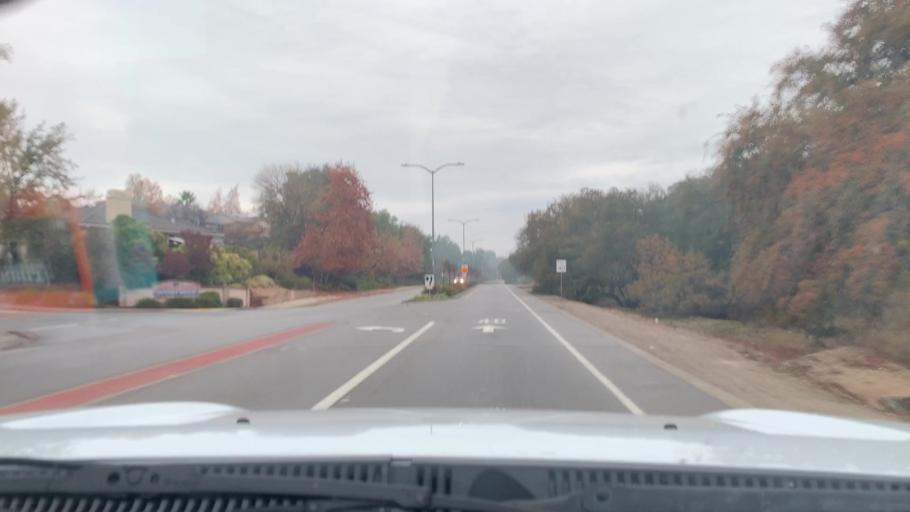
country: US
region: California
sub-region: San Luis Obispo County
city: Paso Robles
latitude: 35.6337
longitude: -120.6731
